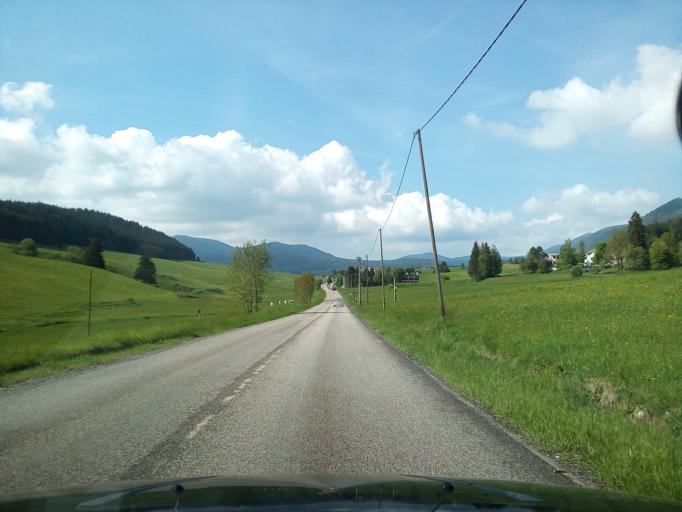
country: FR
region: Rhone-Alpes
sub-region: Departement de l'Isere
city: Autrans
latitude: 45.1574
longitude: 5.5530
